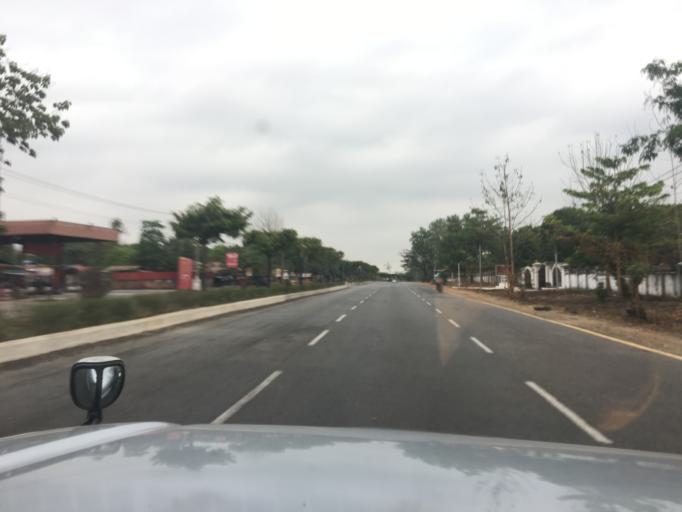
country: MM
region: Bago
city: Thanatpin
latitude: 17.1995
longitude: 96.4034
